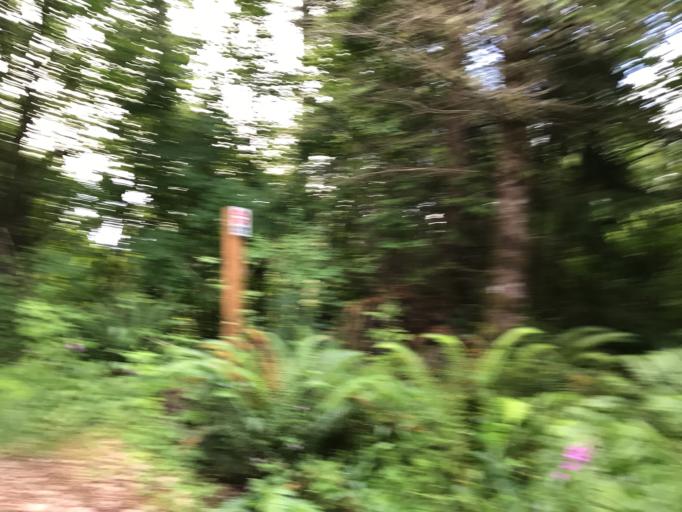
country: US
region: Washington
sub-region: King County
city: Ravensdale
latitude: 47.3430
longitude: -122.0058
